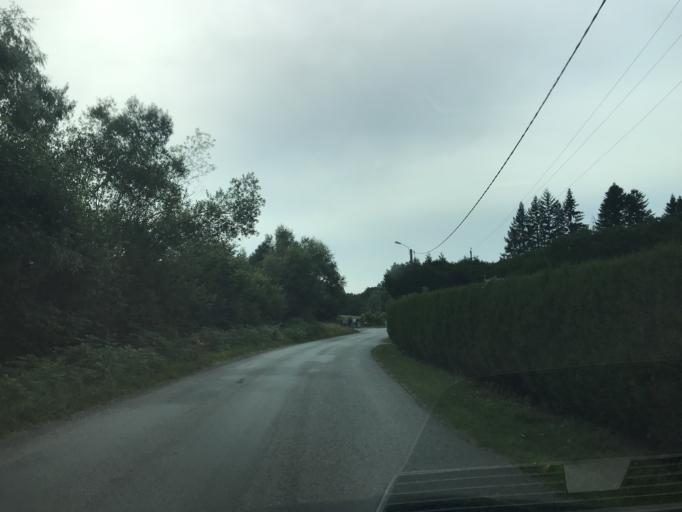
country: FR
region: Limousin
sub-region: Departement de la Correze
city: Neuvic
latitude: 45.3737
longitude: 2.2426
